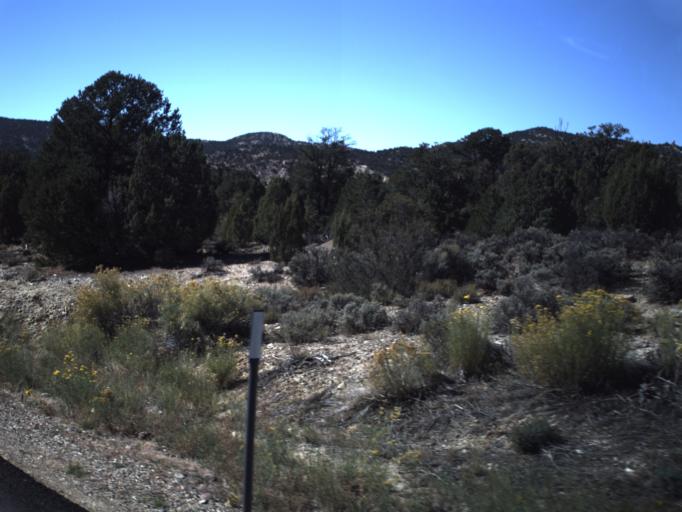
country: US
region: Utah
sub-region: Garfield County
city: Panguitch
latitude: 37.6175
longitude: -111.8805
